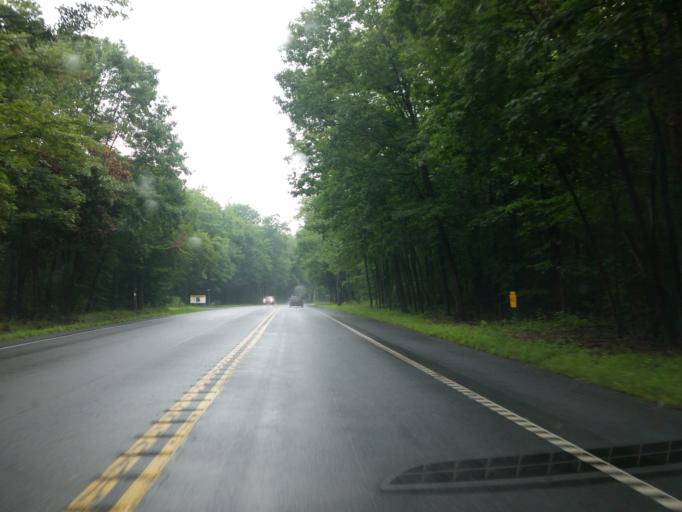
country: US
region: Pennsylvania
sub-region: Lebanon County
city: Palmyra
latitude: 40.4263
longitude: -76.6023
